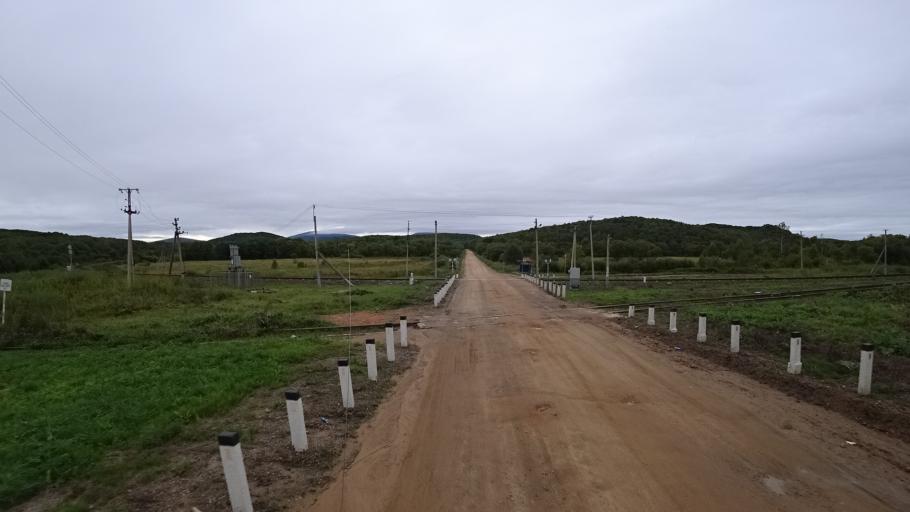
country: RU
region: Primorskiy
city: Rettikhovka
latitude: 44.1733
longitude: 132.8785
